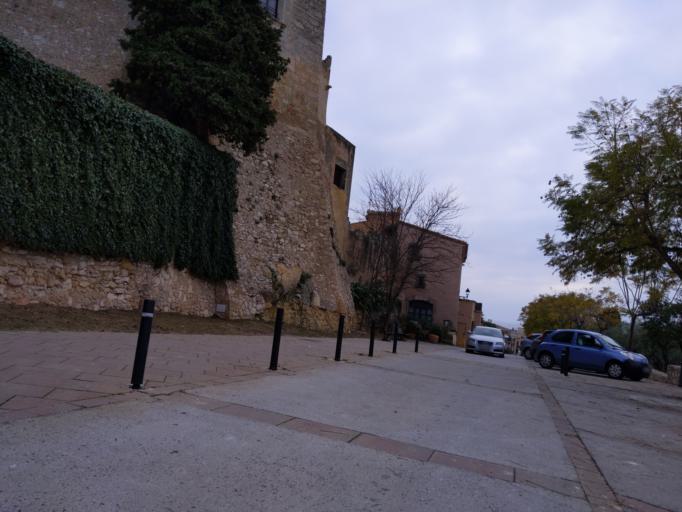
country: ES
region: Catalonia
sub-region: Provincia de Tarragona
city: Altafulla
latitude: 41.1430
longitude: 1.3756
